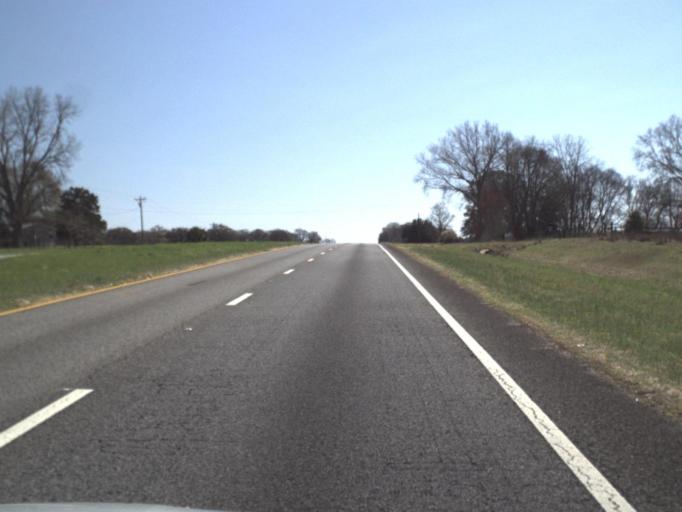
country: US
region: Florida
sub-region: Jackson County
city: Graceville
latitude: 30.8968
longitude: -85.3721
